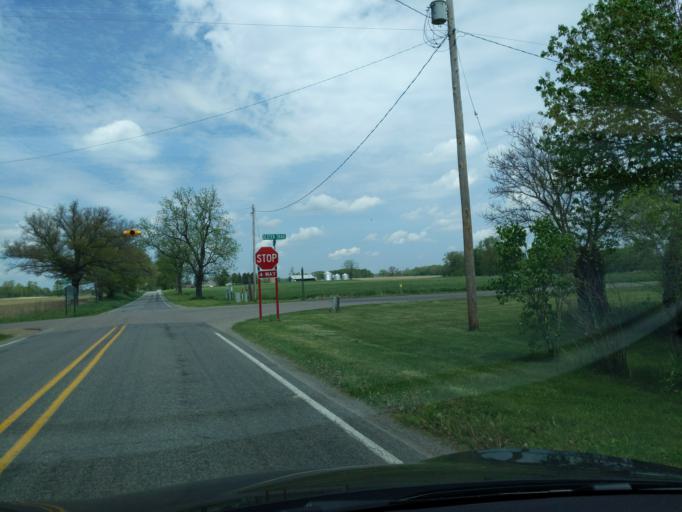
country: US
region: Michigan
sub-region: Ingham County
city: Stockbridge
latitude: 42.4680
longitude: -84.1603
